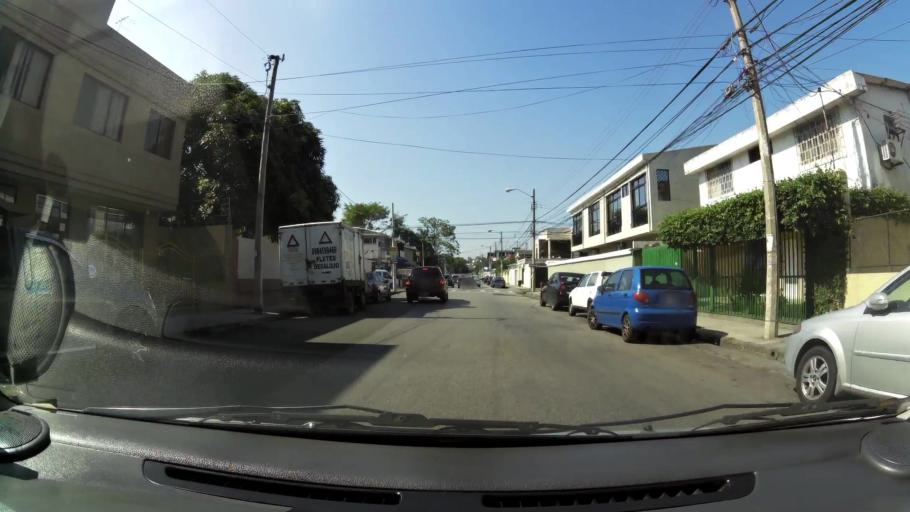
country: EC
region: Guayas
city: Guayaquil
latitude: -2.1651
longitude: -79.9190
